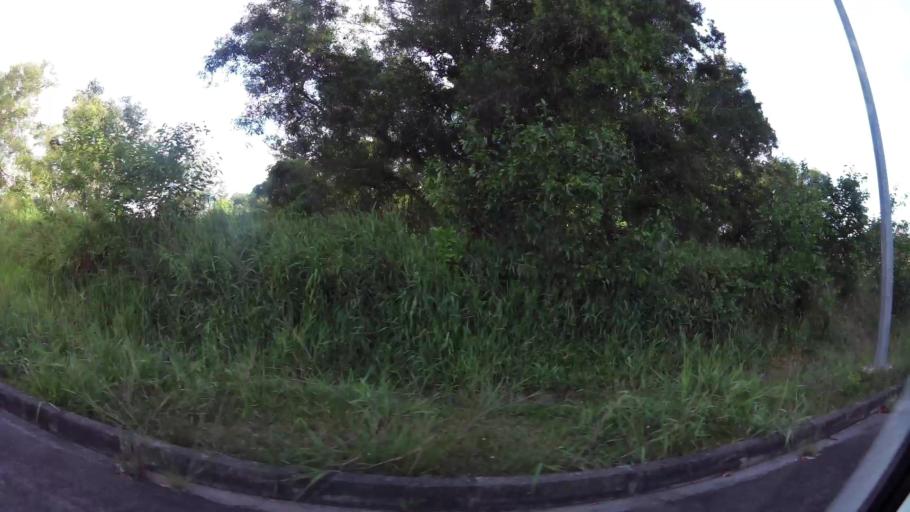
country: BN
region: Brunei and Muara
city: Bandar Seri Begawan
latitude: 4.9817
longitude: 114.9610
